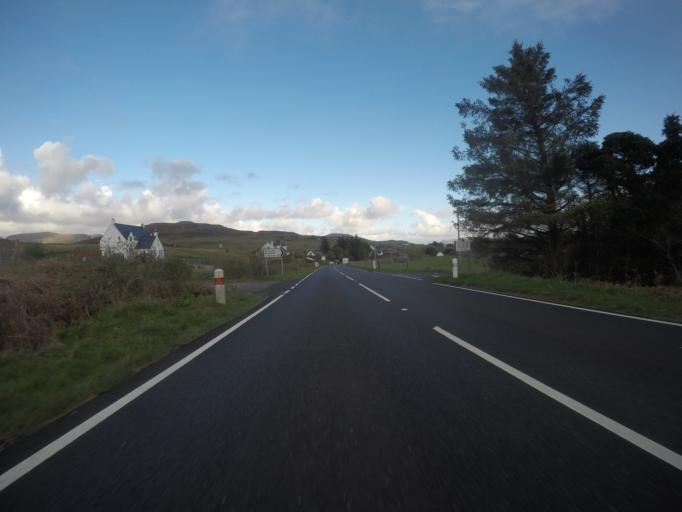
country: GB
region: Scotland
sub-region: Highland
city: Portree
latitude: 57.4998
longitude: -6.3262
